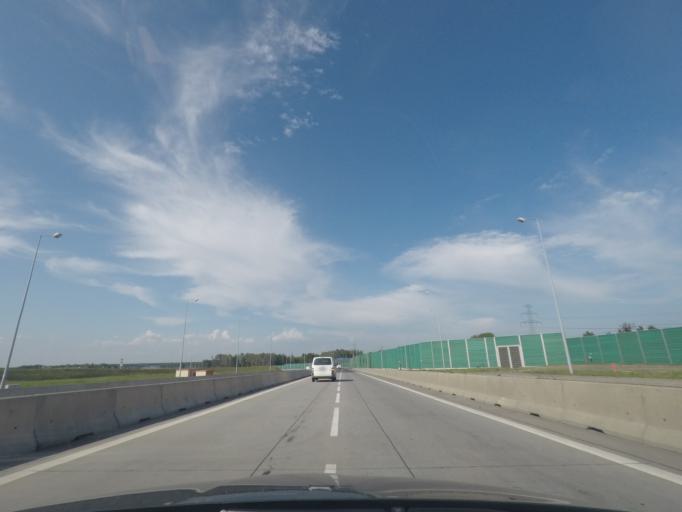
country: PL
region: Silesian Voivodeship
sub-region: Zory
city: Zory
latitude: 50.0671
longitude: 18.6637
